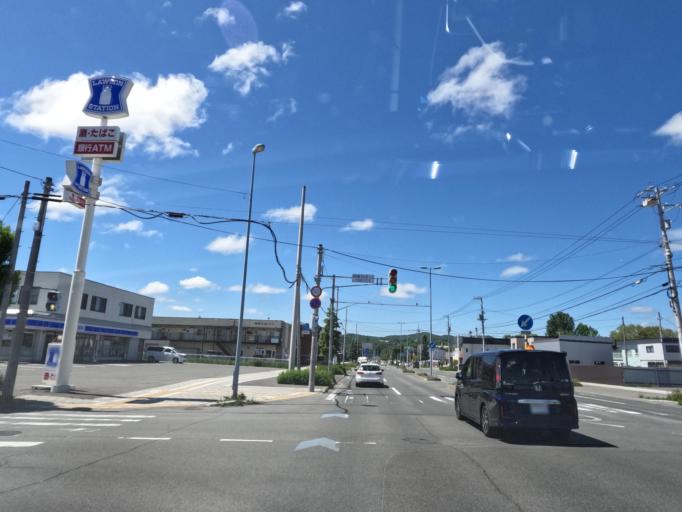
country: JP
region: Hokkaido
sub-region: Asahikawa-shi
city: Asahikawa
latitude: 43.7589
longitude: 142.3565
